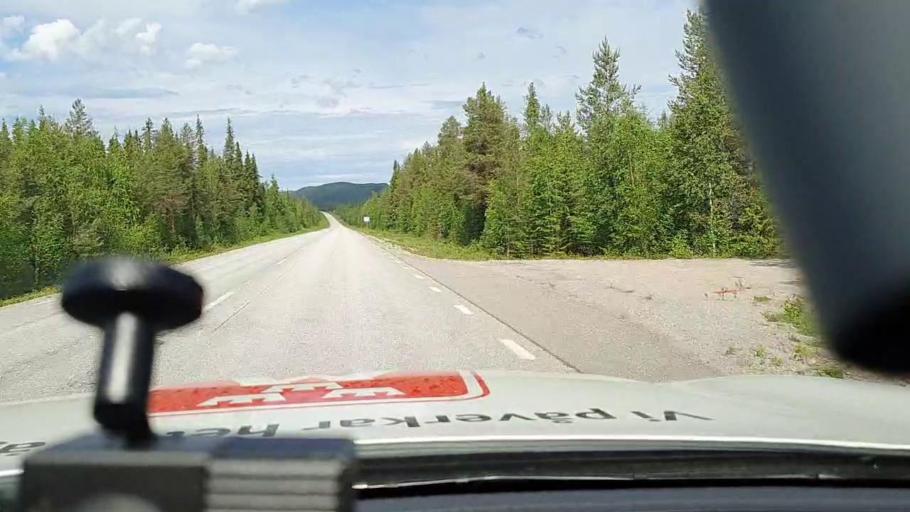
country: SE
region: Norrbotten
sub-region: Jokkmokks Kommun
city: Jokkmokk
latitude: 66.5452
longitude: 20.1353
